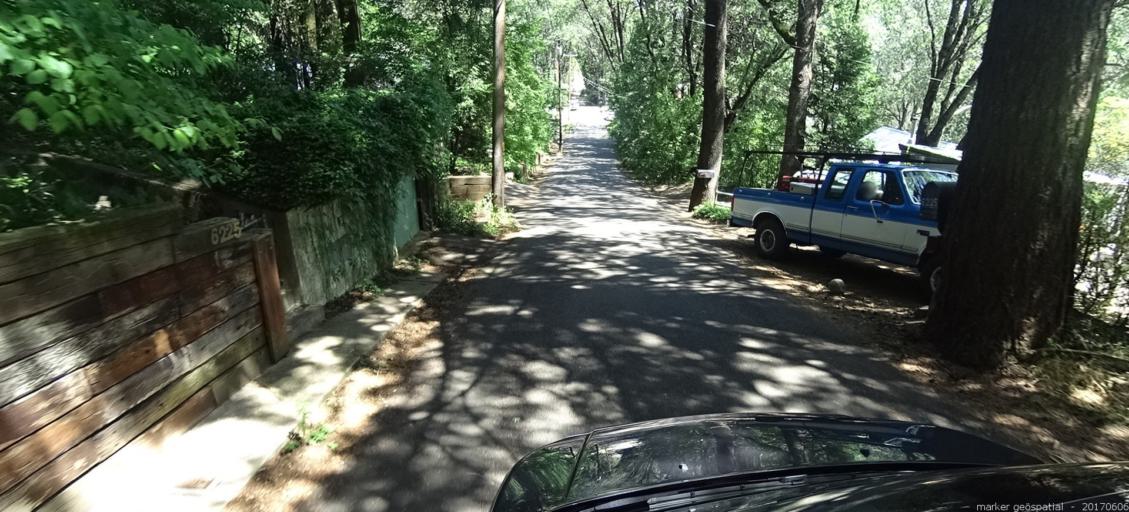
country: US
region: California
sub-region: Siskiyou County
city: Dunsmuir
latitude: 41.2037
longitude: -122.2760
